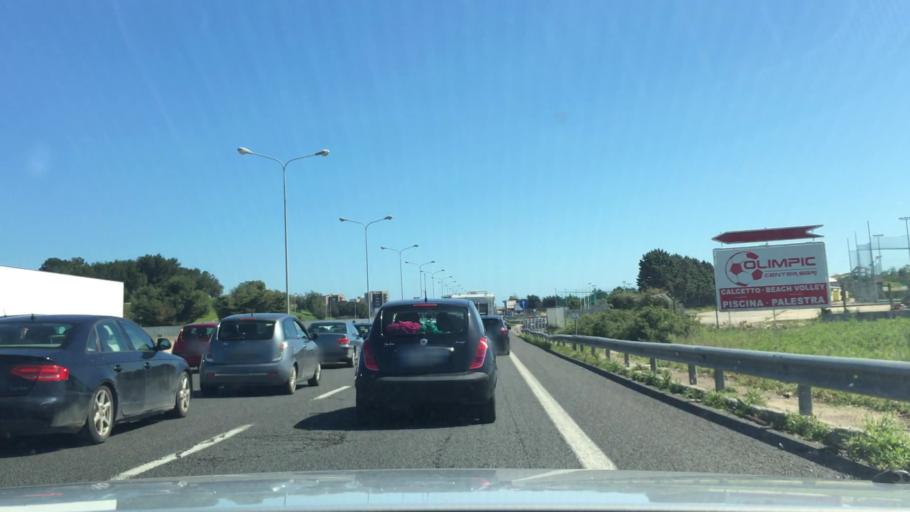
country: IT
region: Apulia
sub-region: Provincia di Bari
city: Triggiano
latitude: 41.0978
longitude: 16.9023
